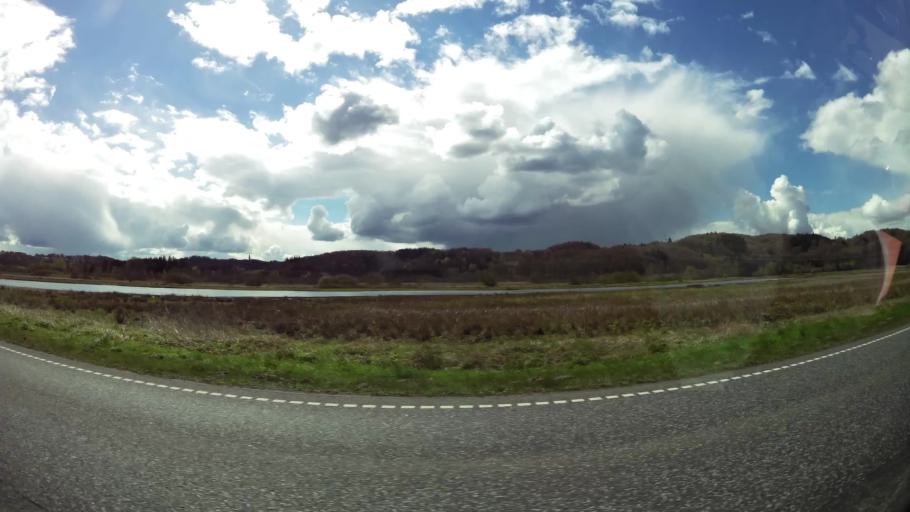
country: DK
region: South Denmark
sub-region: Vejle Kommune
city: Vejle
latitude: 55.7076
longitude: 9.4848
